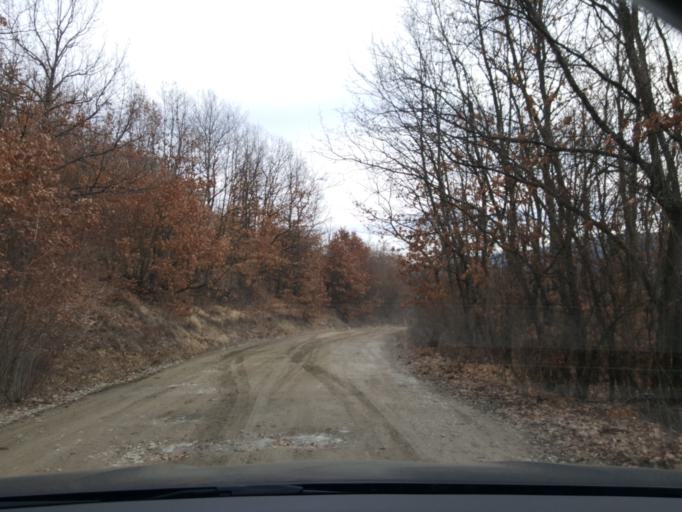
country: RS
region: Central Serbia
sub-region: Pirotski Okrug
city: Dimitrovgrad
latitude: 42.9979
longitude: 22.7475
